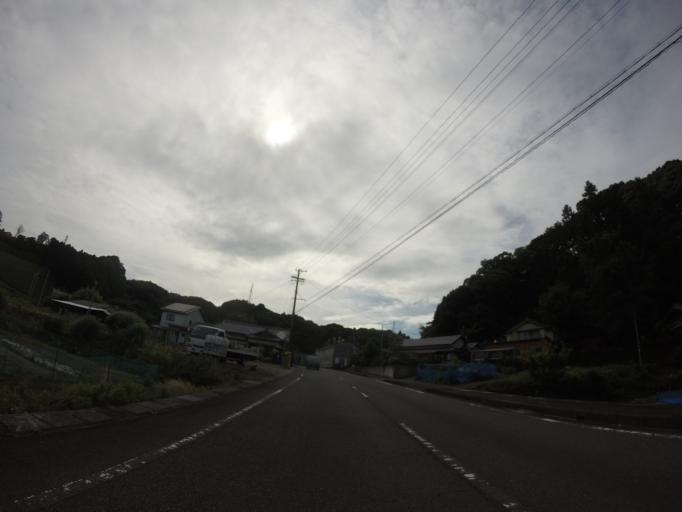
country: JP
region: Shizuoka
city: Kanaya
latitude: 34.7870
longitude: 138.1520
